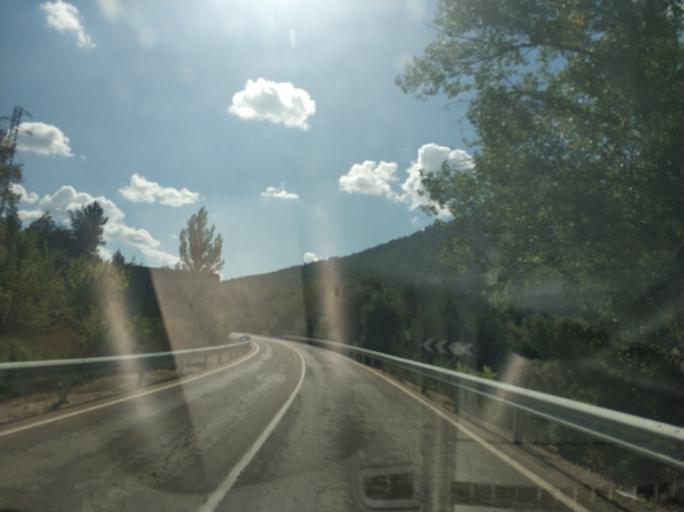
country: ES
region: Castille and Leon
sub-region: Provincia de Soria
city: San Leonardo de Yague
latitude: 41.8240
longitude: -3.0730
